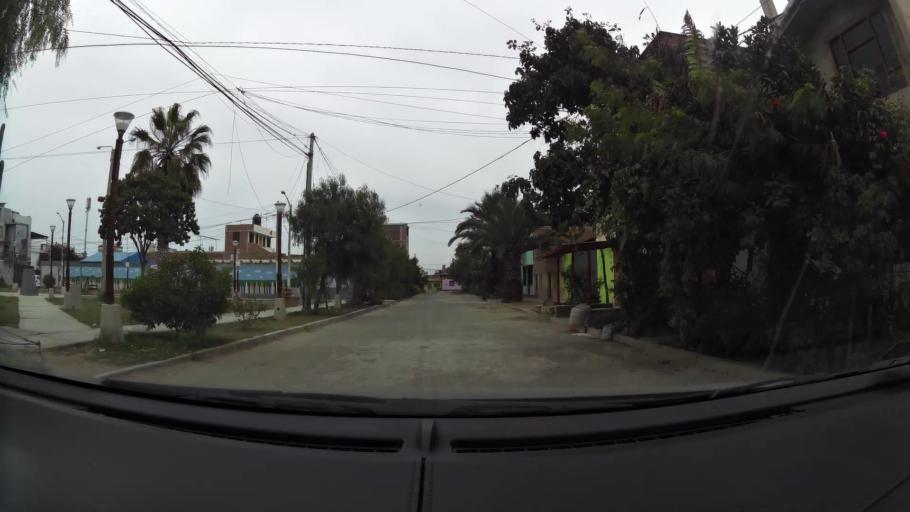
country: PE
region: La Libertad
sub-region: Provincia de Trujillo
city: Buenos Aires
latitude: -8.1422
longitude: -79.0460
